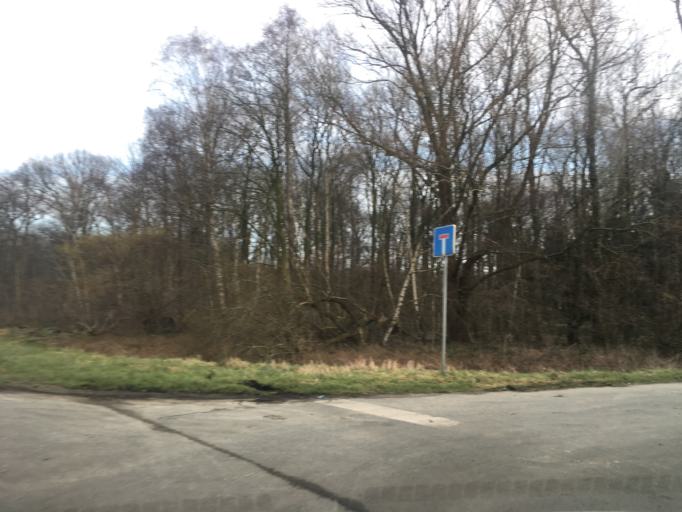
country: DE
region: North Rhine-Westphalia
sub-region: Regierungsbezirk Munster
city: Dulmen
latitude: 51.8494
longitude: 7.3077
